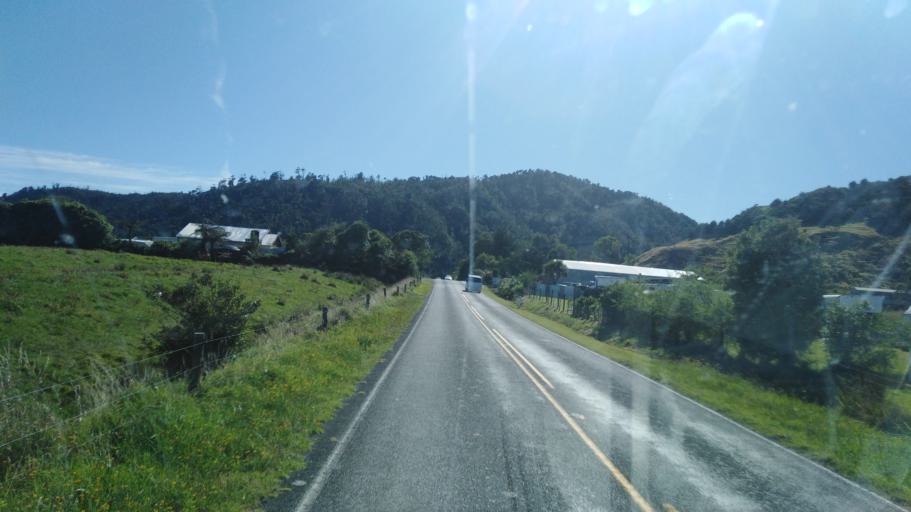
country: NZ
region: West Coast
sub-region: Buller District
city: Westport
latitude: -41.5324
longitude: 171.9386
